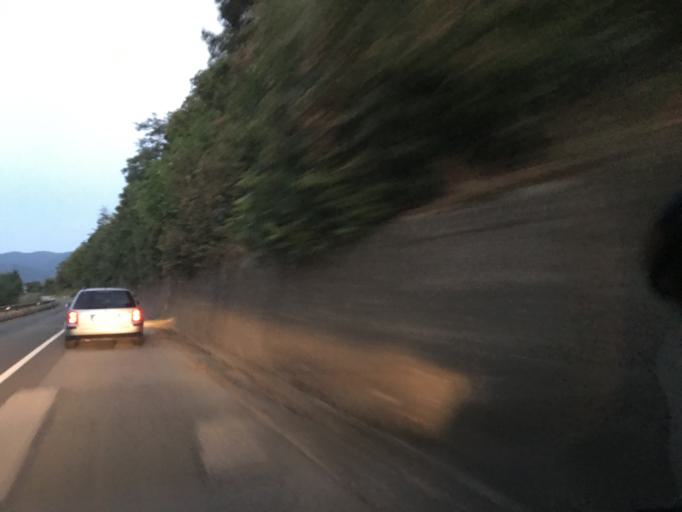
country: RO
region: Caras-Severin
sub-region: Comuna Berzasca
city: Liubcova
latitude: 44.6403
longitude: 21.9194
